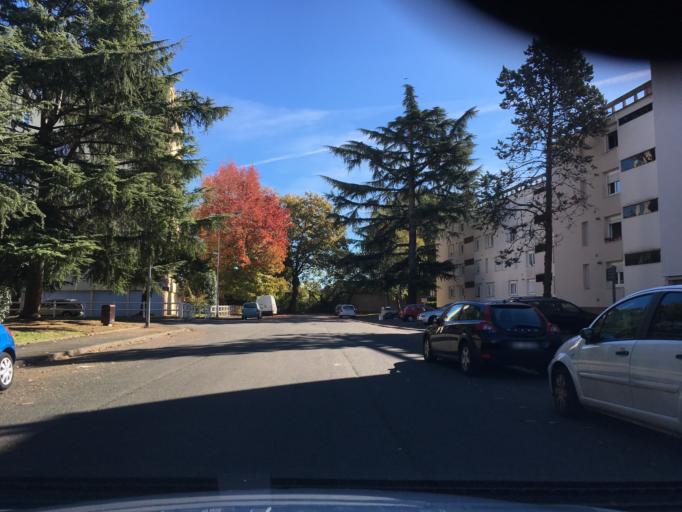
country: FR
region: Aquitaine
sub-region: Departement des Pyrenees-Atlantiques
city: Pau
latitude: 43.3154
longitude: -0.3434
